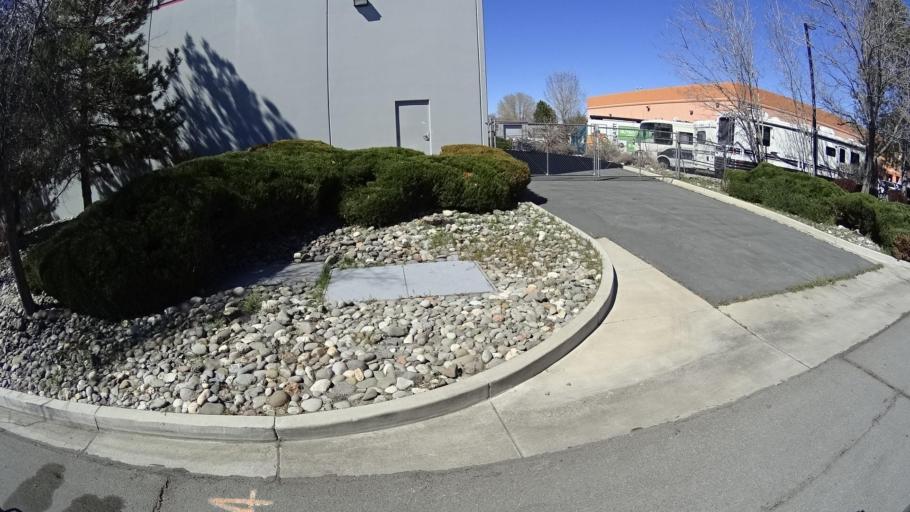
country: US
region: Nevada
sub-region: Washoe County
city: Sparks
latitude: 39.4711
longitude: -119.7706
